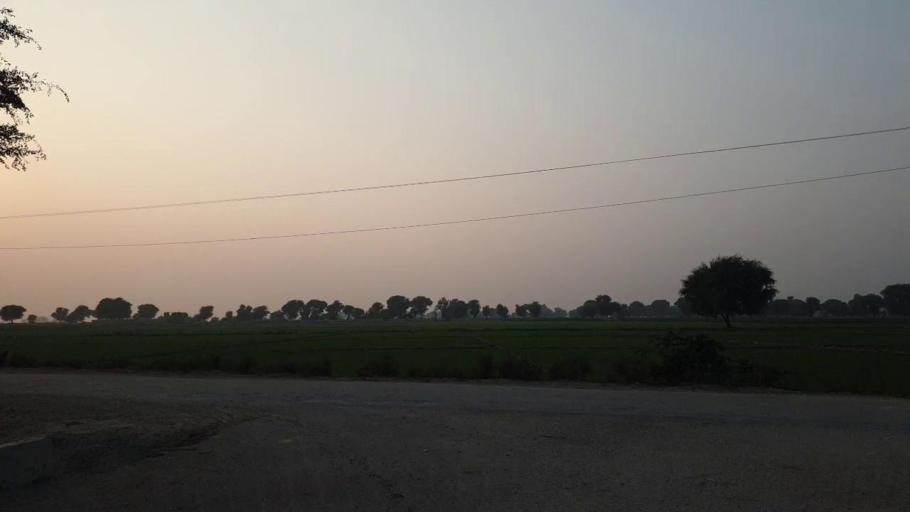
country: PK
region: Sindh
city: Bhan
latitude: 26.5309
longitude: 67.6960
